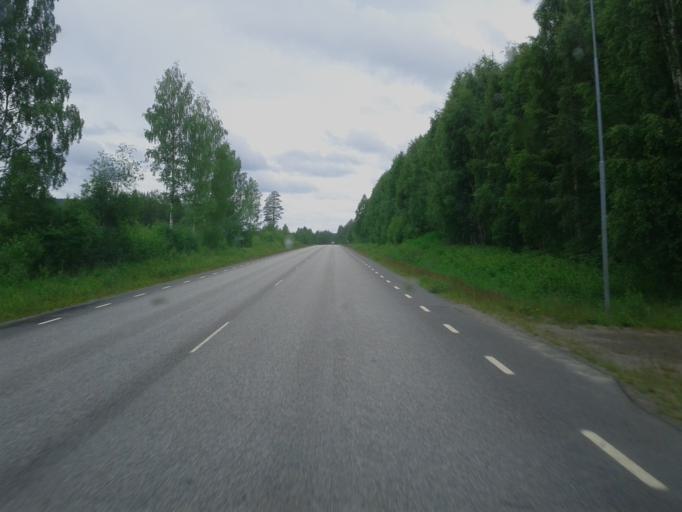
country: SE
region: Vaesterbotten
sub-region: Skelleftea Kommun
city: Langsele
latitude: 64.9179
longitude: 20.0928
